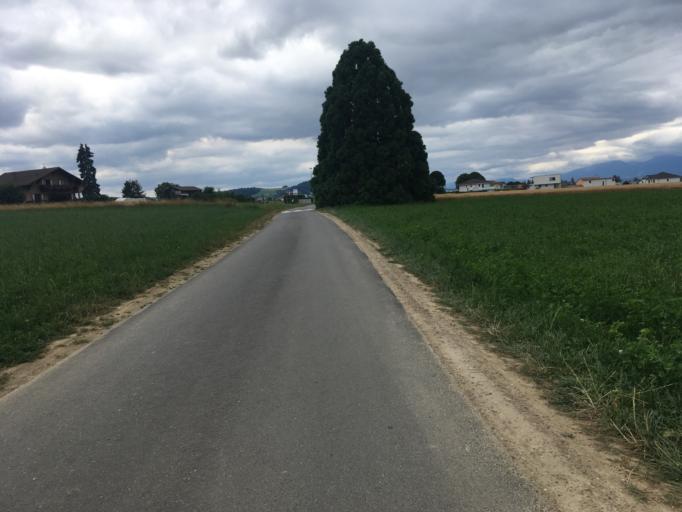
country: CH
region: Fribourg
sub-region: Broye District
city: Estavayer-le-Lac
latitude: 46.8551
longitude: 6.8644
